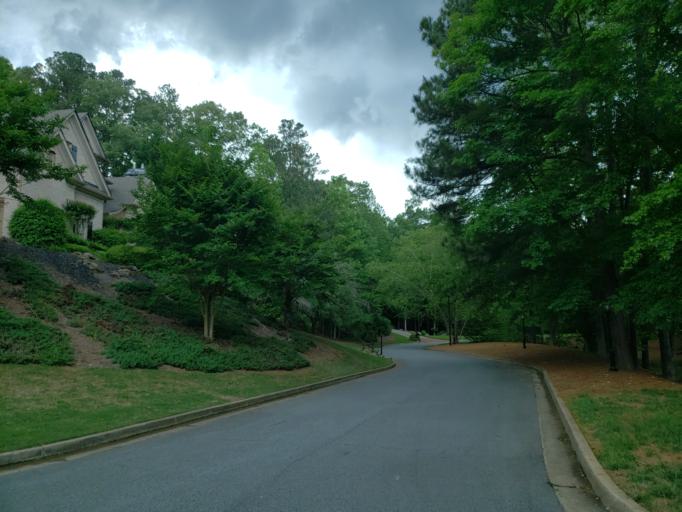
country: US
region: Georgia
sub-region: Cobb County
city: Marietta
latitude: 33.9570
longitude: -84.5773
